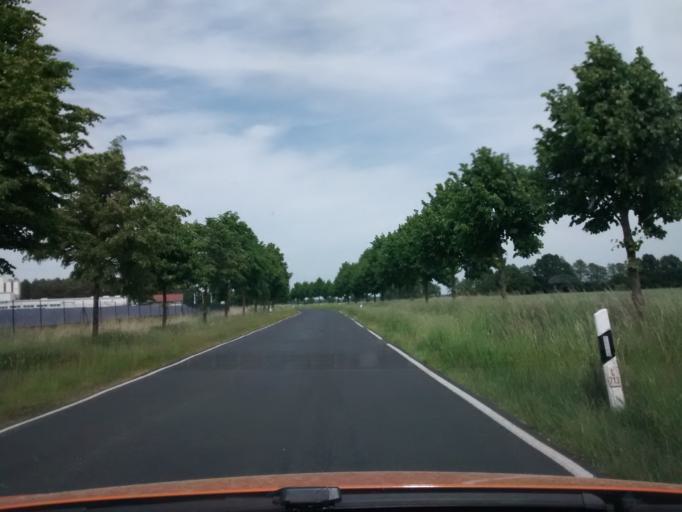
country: DE
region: Saxony-Anhalt
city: Holzdorf
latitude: 51.8207
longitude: 13.2345
